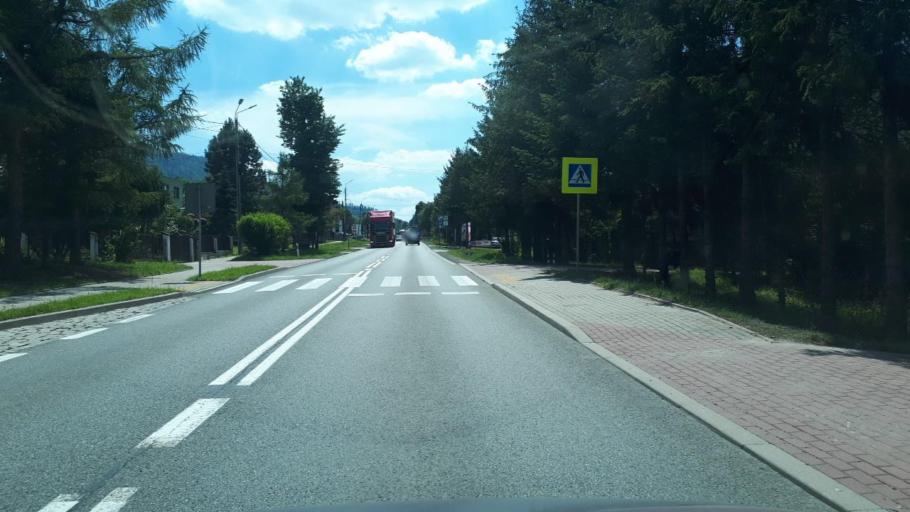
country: PL
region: Silesian Voivodeship
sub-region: Powiat bielski
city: Kozy
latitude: 49.8330
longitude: 19.1241
